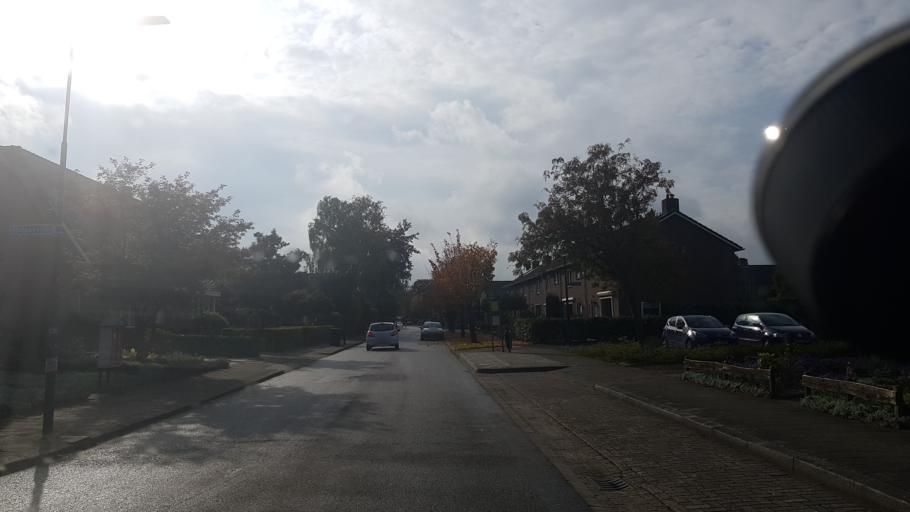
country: NL
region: Gelderland
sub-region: Gemeente Apeldoorn
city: Beekbergen
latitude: 52.1838
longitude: 5.9380
